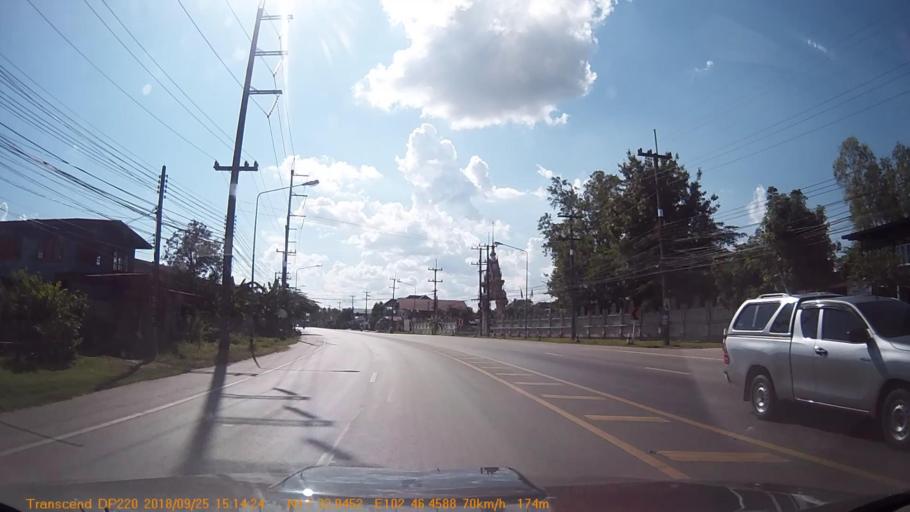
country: TH
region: Changwat Udon Thani
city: Udon Thani
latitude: 17.5342
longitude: 102.7738
